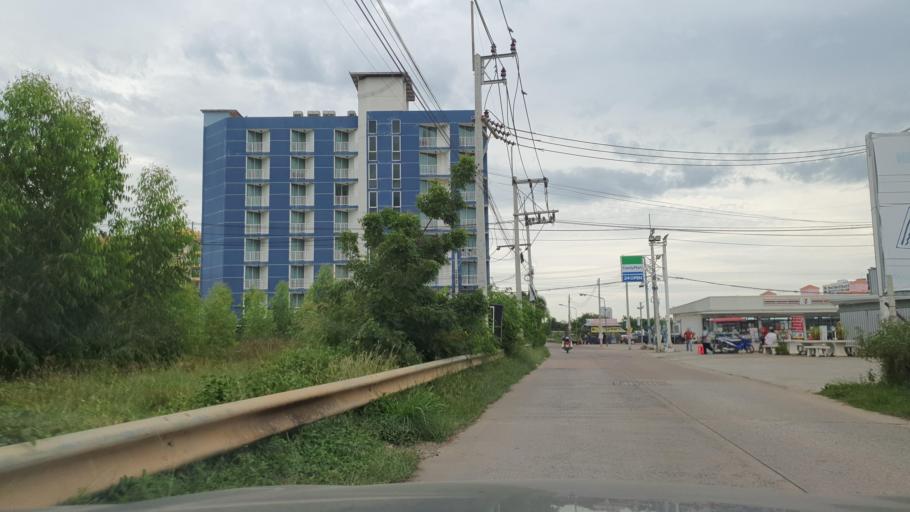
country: TH
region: Chon Buri
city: Phatthaya
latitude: 12.8651
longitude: 100.9009
